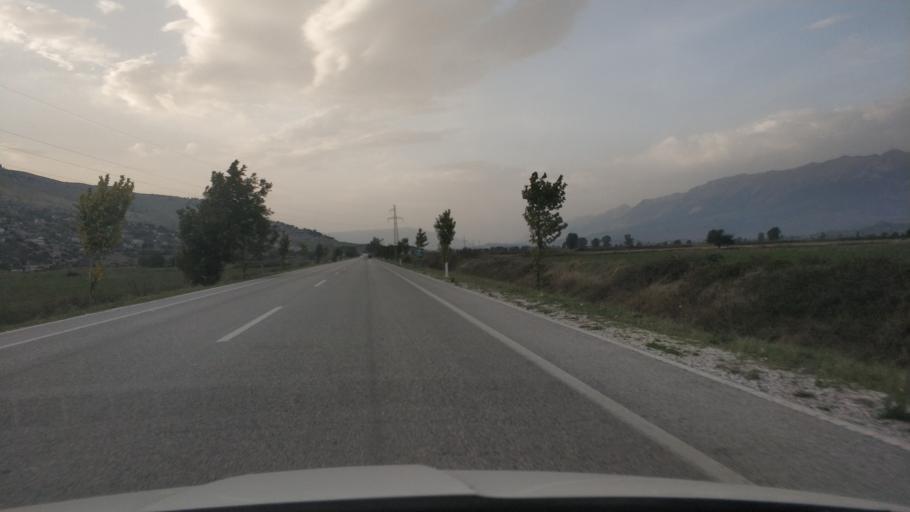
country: AL
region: Gjirokaster
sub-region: Rrethi i Gjirokastres
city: Libohove
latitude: 39.9586
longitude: 20.2473
